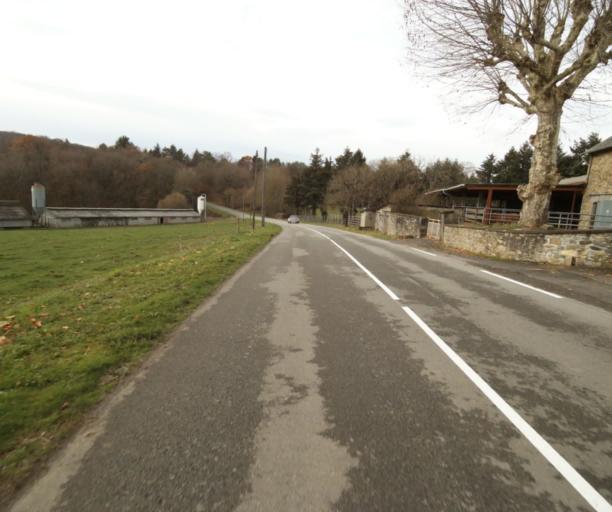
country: FR
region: Limousin
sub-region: Departement de la Correze
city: Chameyrat
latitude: 45.2649
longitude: 1.7090
